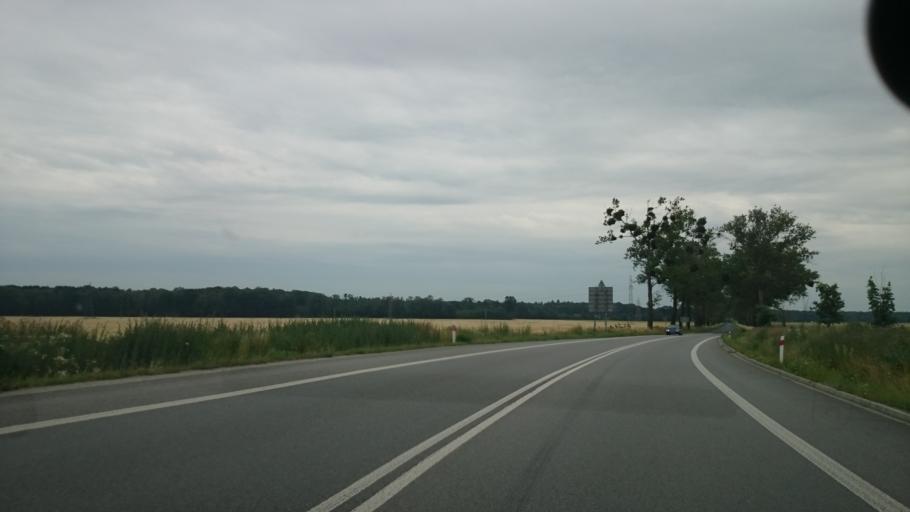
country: PL
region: Opole Voivodeship
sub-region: Powiat brzeski
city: Grodkow
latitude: 50.6819
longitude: 17.4037
